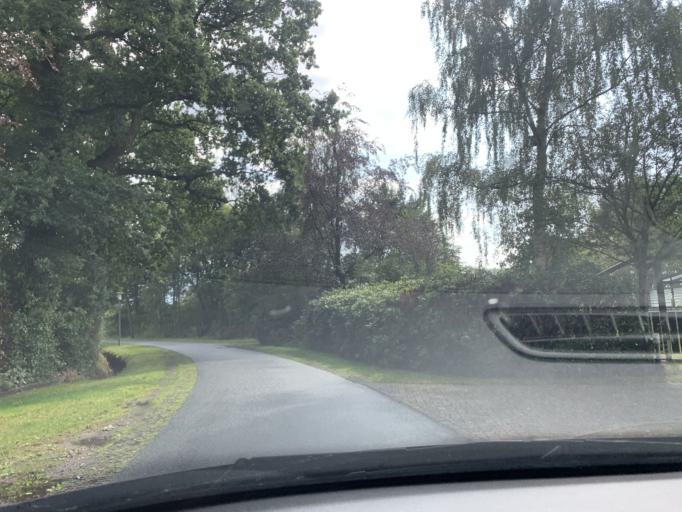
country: DE
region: Lower Saxony
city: Westerstede
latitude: 53.2664
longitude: 7.8999
